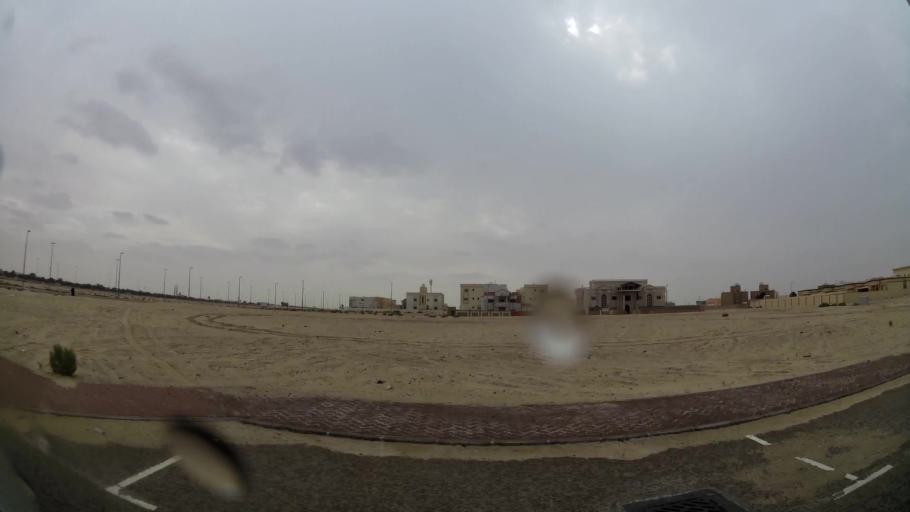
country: AE
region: Abu Dhabi
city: Abu Dhabi
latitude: 24.3647
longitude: 54.6474
